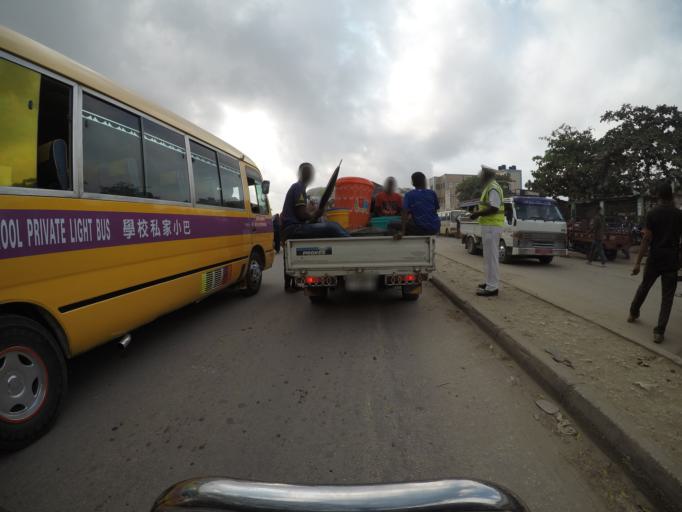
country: TZ
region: Zanzibar Urban/West
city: Zanzibar
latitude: -6.1772
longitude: 39.2254
